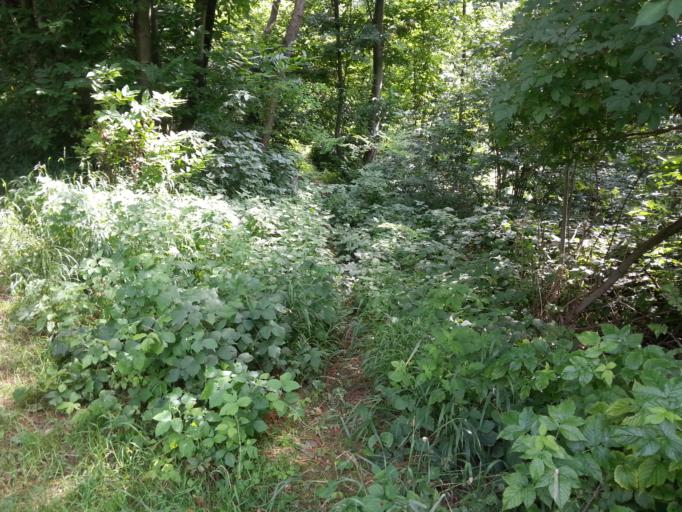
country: IT
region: Lombardy
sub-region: Provincia di Lecco
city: Ballabio
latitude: 45.8848
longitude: 9.4215
